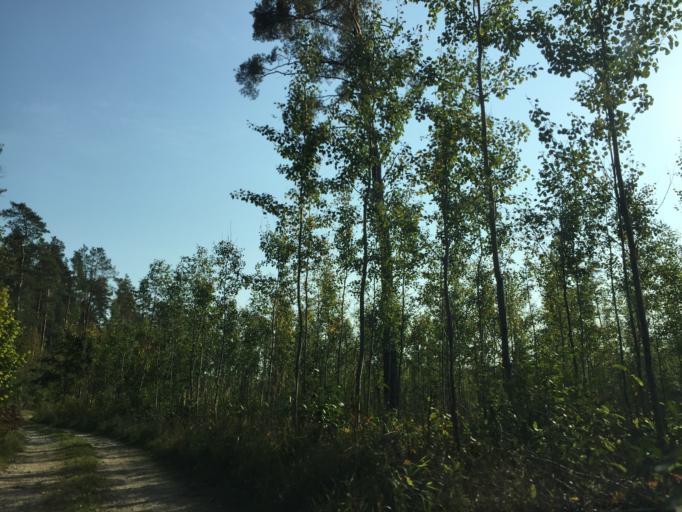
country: LV
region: Ikskile
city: Ikskile
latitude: 56.8895
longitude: 24.4942
